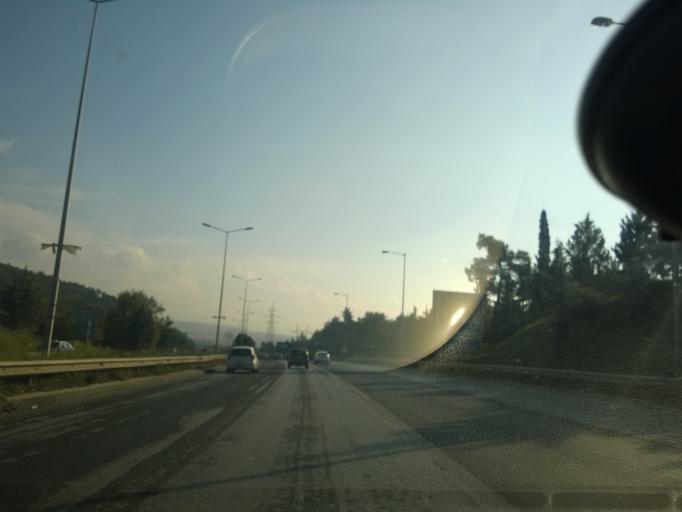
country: GR
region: Central Macedonia
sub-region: Nomos Thessalonikis
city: Agios Pavlos
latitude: 40.6398
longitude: 22.9699
